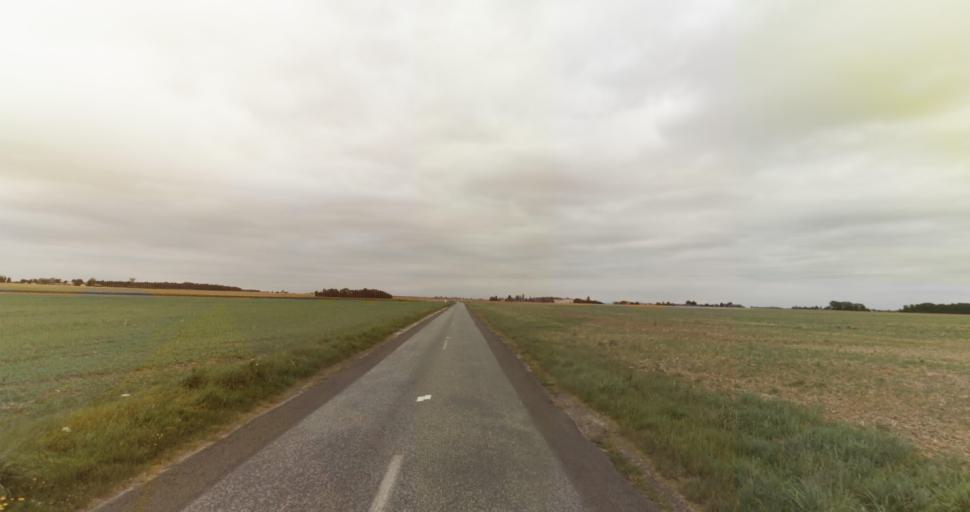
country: FR
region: Haute-Normandie
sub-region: Departement de l'Eure
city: Marcilly-sur-Eure
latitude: 48.9115
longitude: 1.2848
